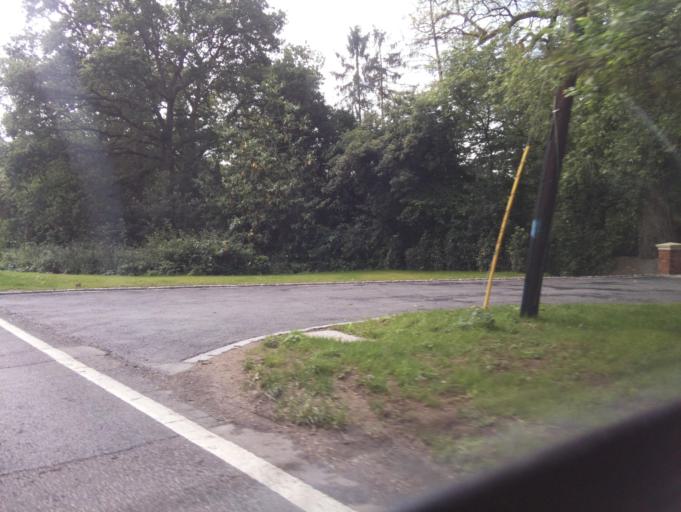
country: GB
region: England
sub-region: Hampshire
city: Odiham
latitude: 51.2505
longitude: -0.8990
